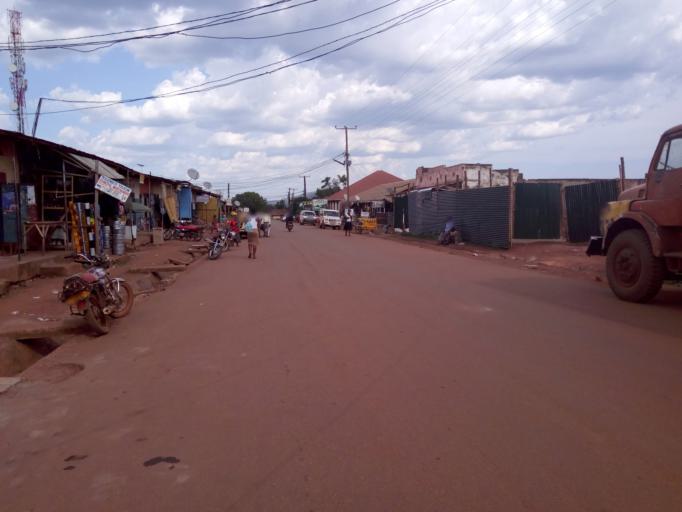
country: UG
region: Western Region
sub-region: Masindi District
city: Masindi
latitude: 1.6818
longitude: 31.7212
